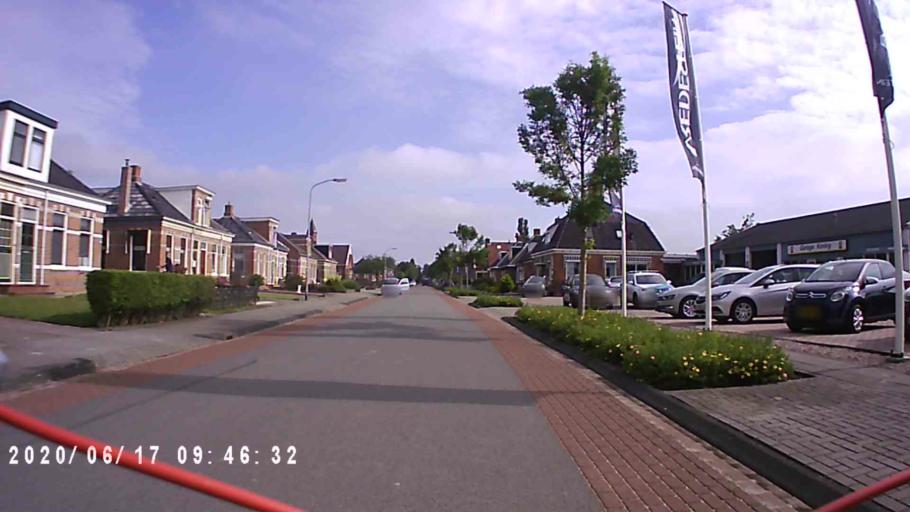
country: NL
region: Groningen
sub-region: Gemeente De Marne
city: Ulrum
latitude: 53.3557
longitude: 6.3379
